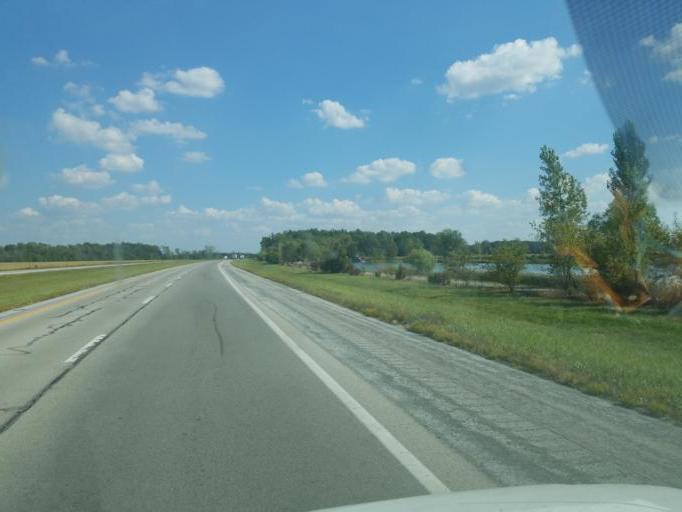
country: US
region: Ohio
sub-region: Allen County
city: Elida
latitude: 40.8344
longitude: -84.1657
